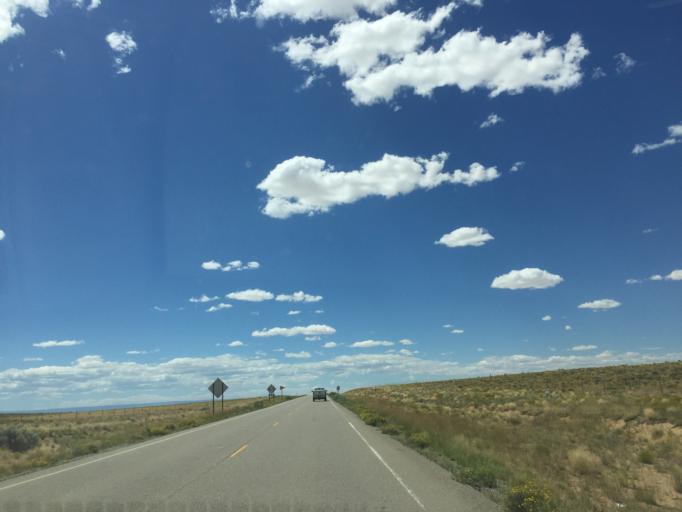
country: US
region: New Mexico
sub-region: San Juan County
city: Upper Fruitland
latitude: 36.4372
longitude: -108.2550
